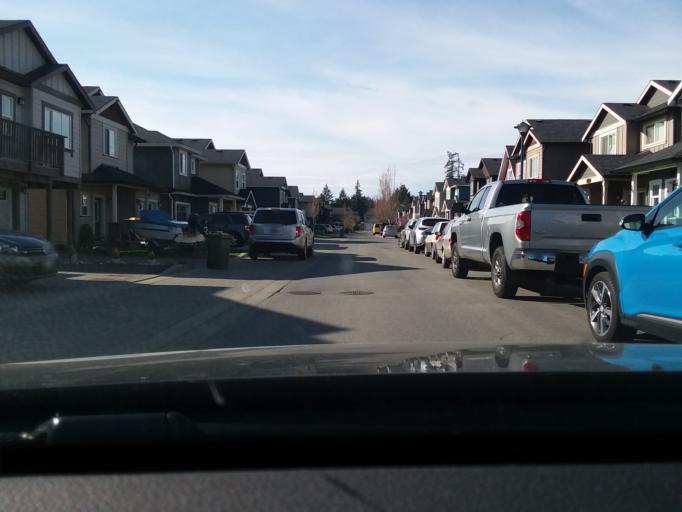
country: CA
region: British Columbia
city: Langford
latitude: 48.4270
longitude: -123.5333
